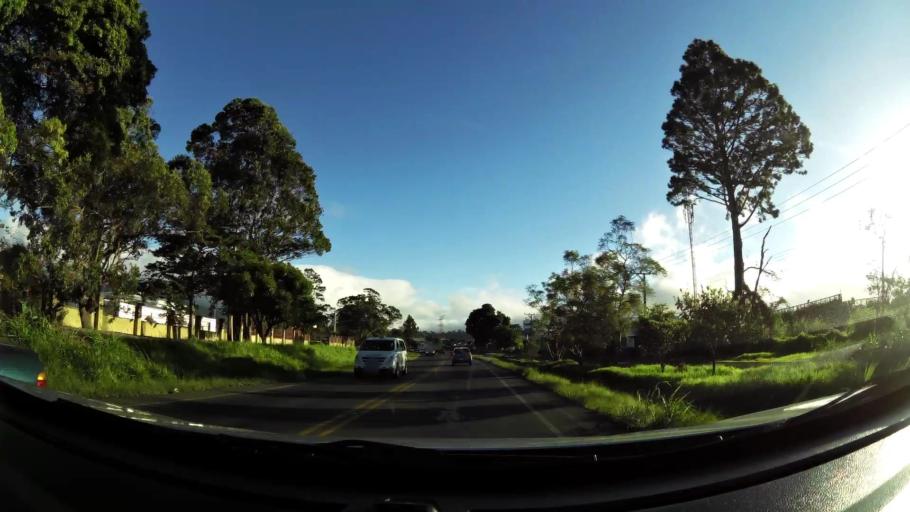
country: CR
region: Heredia
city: Angeles
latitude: 9.9924
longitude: -84.0385
